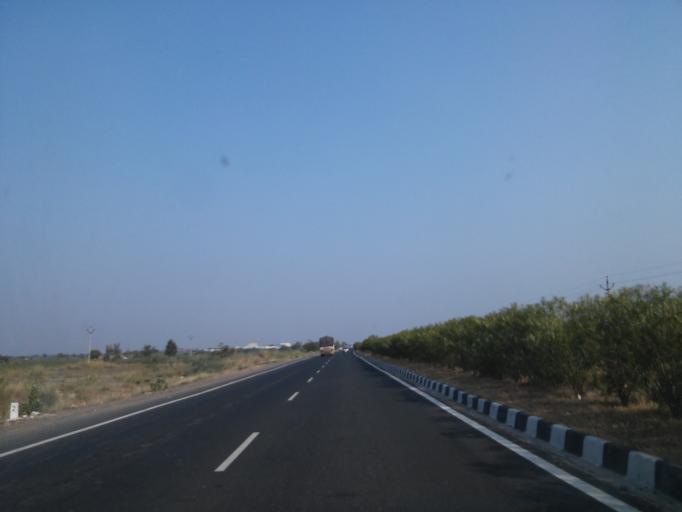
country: IN
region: Gujarat
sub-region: Surendranagar
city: Halvad
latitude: 23.0052
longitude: 71.1302
